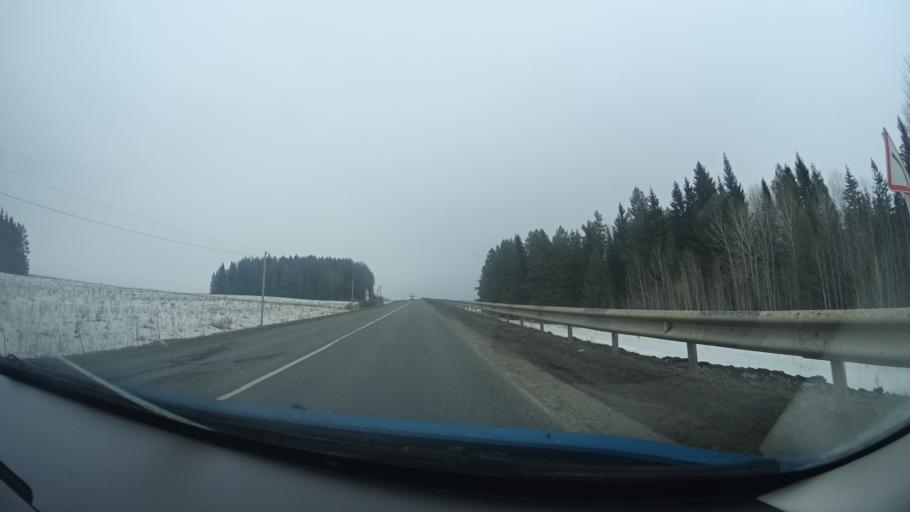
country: RU
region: Perm
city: Osa
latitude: 57.3120
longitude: 55.6211
